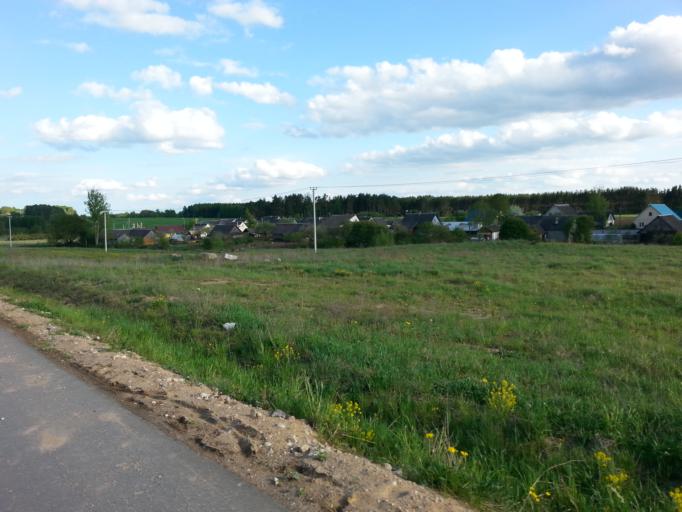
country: BY
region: Minsk
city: Narach
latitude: 54.9362
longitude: 26.7009
